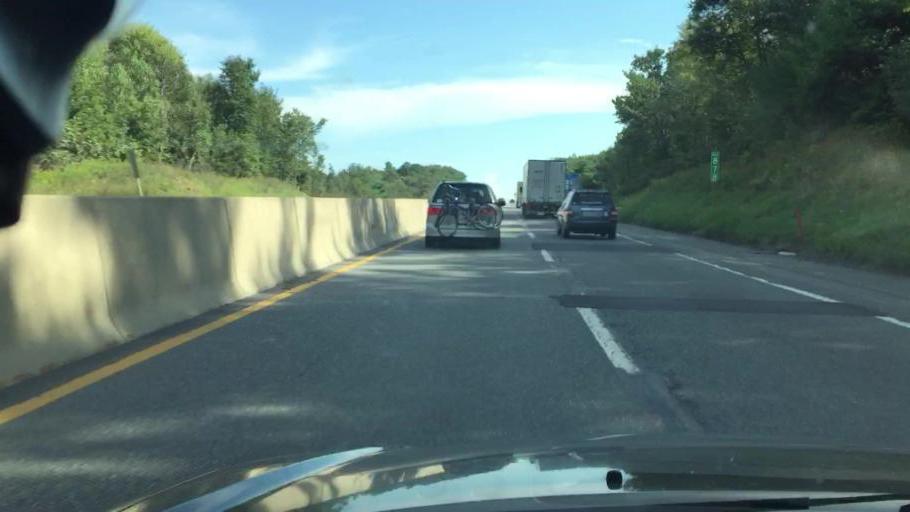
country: US
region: Pennsylvania
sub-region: Carbon County
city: Towamensing Trails
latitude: 40.9936
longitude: -75.6324
